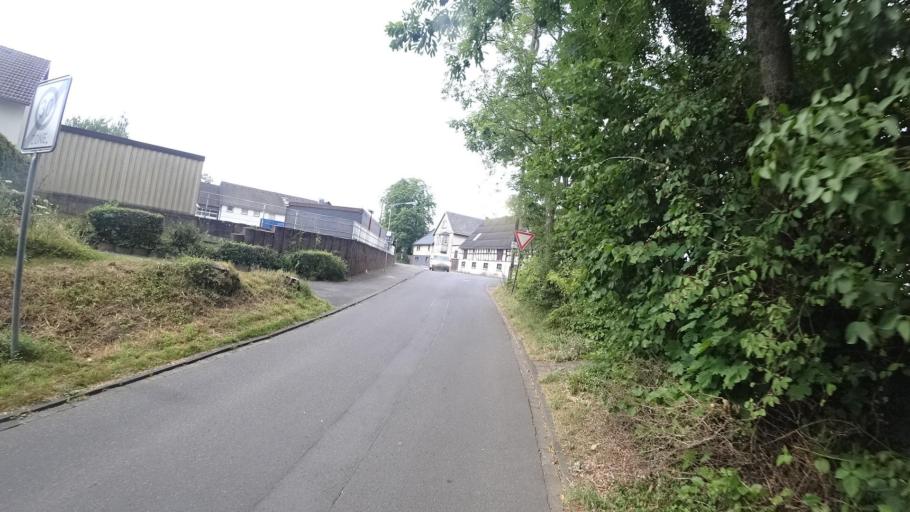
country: DE
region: Rheinland-Pfalz
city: Birnbach
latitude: 50.7080
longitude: 7.5800
